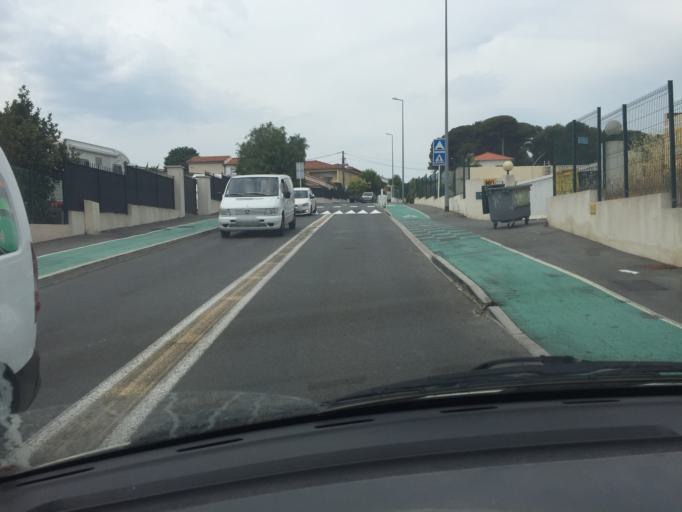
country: FR
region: Provence-Alpes-Cote d'Azur
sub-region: Departement des Alpes-Maritimes
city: Biot
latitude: 43.5960
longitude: 7.0889
